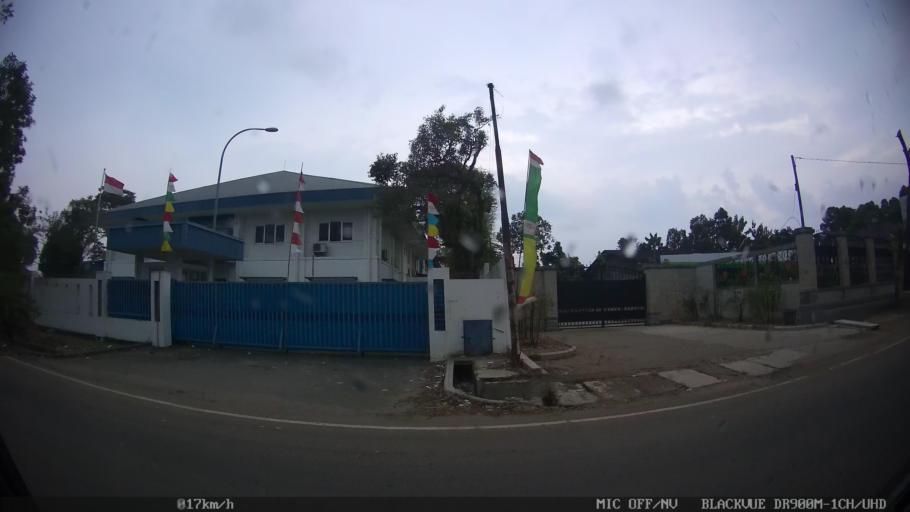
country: ID
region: Lampung
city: Kedaton
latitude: -5.3946
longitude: 105.2813
